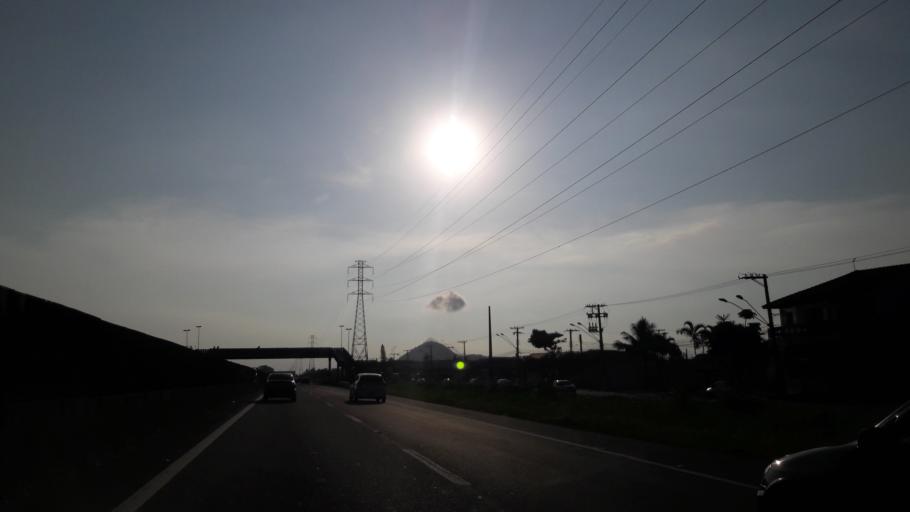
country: BR
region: Sao Paulo
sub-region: Mongagua
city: Mongagua
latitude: -24.1055
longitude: -46.6455
